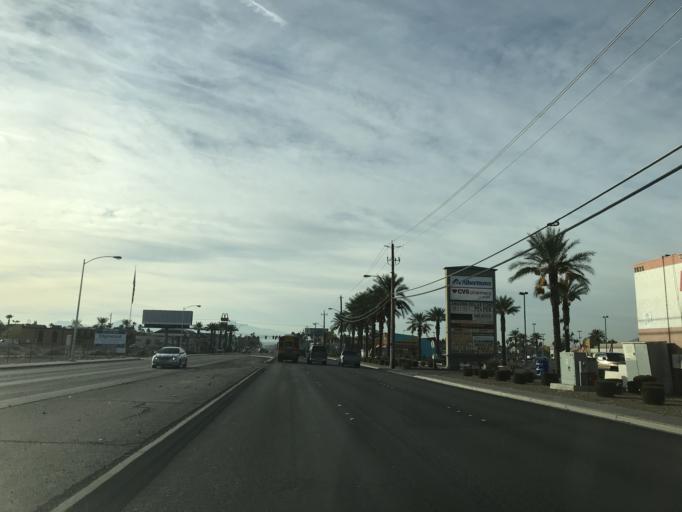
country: US
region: Nevada
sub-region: Clark County
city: Winchester
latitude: 36.1393
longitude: -115.0655
